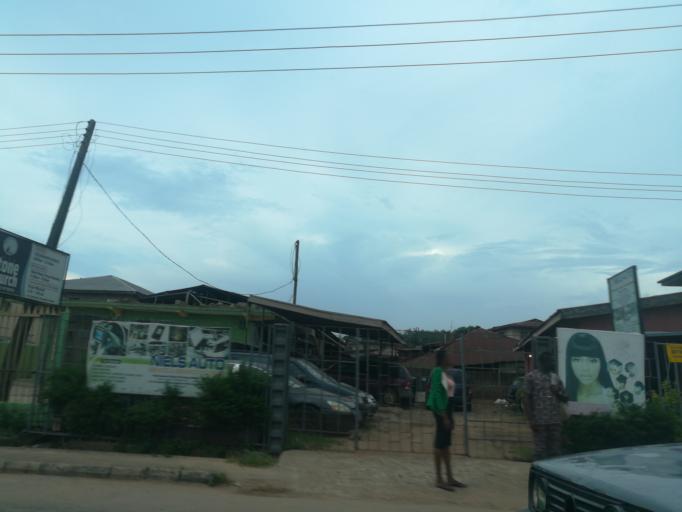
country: NG
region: Oyo
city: Ibadan
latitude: 7.4341
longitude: 3.9071
